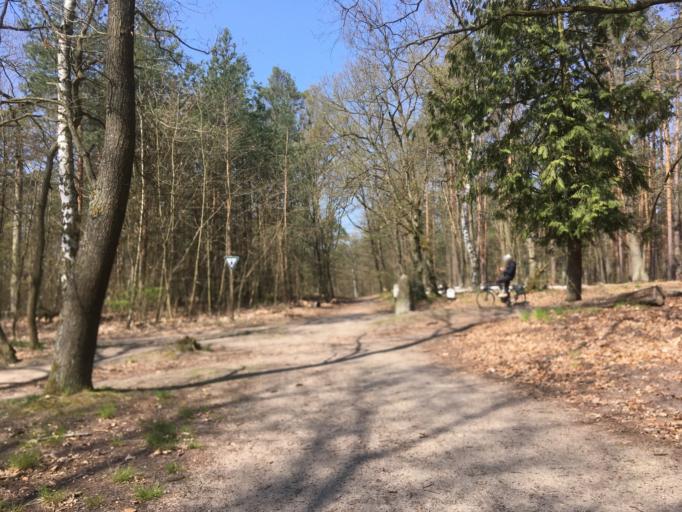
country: DE
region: Berlin
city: Gatow
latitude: 52.4810
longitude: 13.2230
